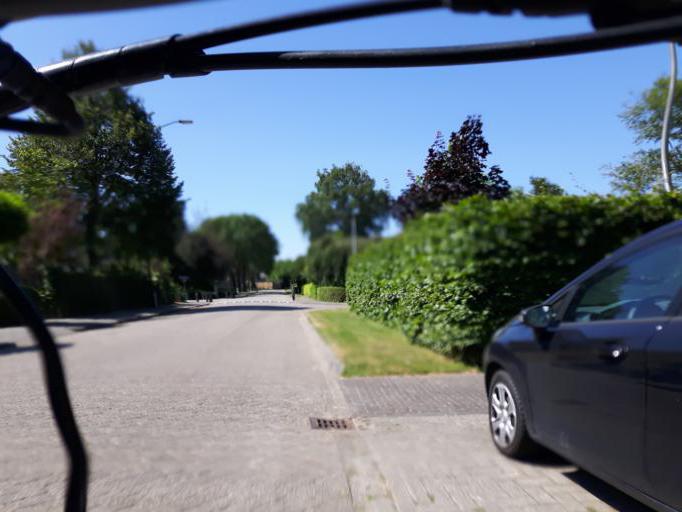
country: NL
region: North Brabant
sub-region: Gemeente Moerdijk
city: Willemstad
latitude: 51.6888
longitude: 4.4458
